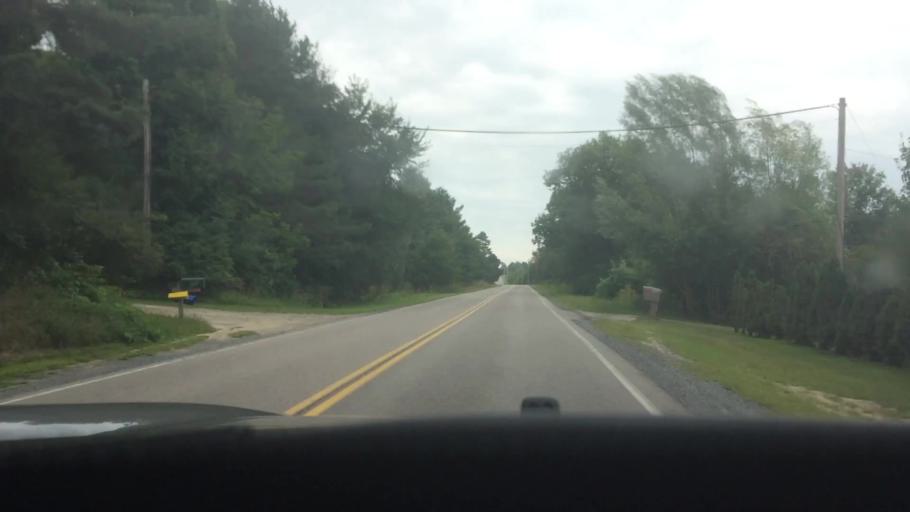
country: US
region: New York
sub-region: St. Lawrence County
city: Hannawa Falls
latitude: 44.5380
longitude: -75.0533
